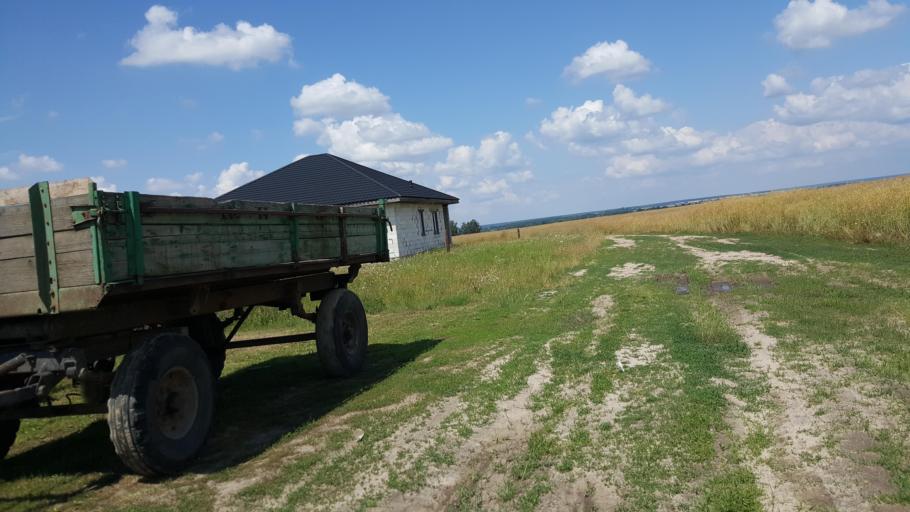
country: BY
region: Brest
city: Kamyanyets
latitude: 52.4049
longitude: 23.8487
